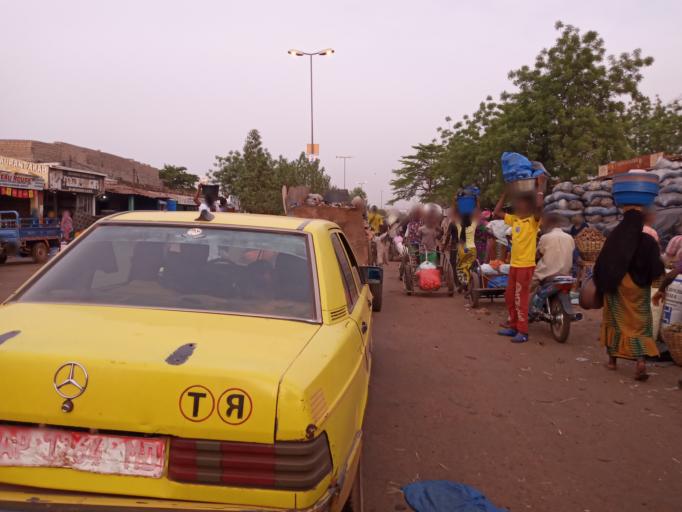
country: ML
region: Bamako
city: Bamako
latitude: 12.6596
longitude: -7.9845
